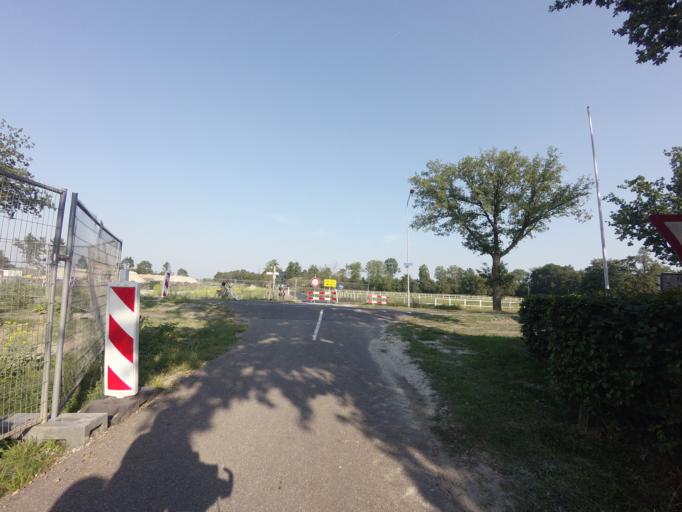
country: NL
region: Groningen
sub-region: Gemeente Groningen
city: Groningen
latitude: 53.1656
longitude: 6.4958
